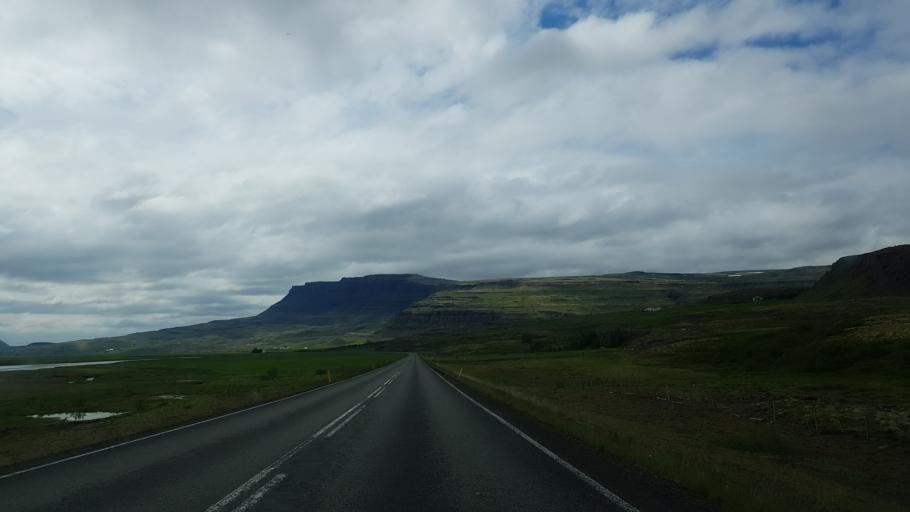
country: IS
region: West
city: Borgarnes
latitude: 64.8047
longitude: -21.4393
